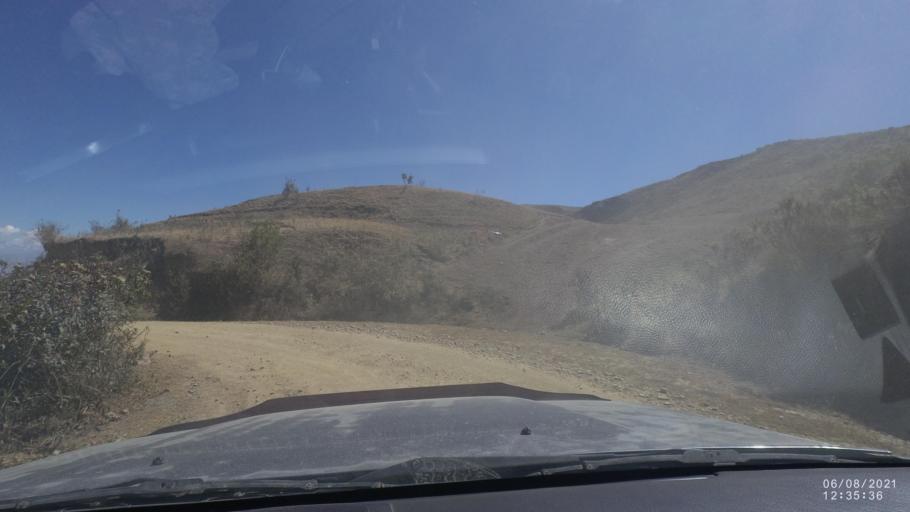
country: BO
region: Cochabamba
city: Colchani
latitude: -16.7784
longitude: -66.6496
